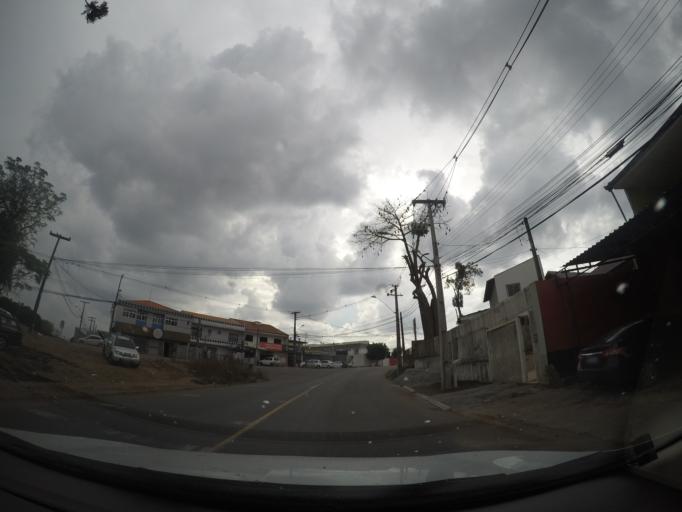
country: BR
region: Parana
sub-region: Sao Jose Dos Pinhais
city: Sao Jose dos Pinhais
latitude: -25.5435
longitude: -49.2419
